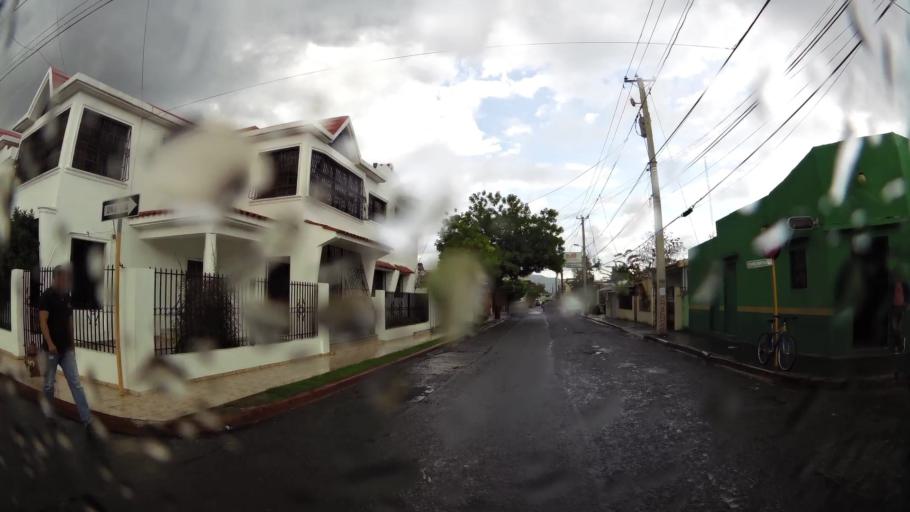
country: DO
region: Monsenor Nouel
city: Bonao
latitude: 18.9435
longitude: -70.4085
